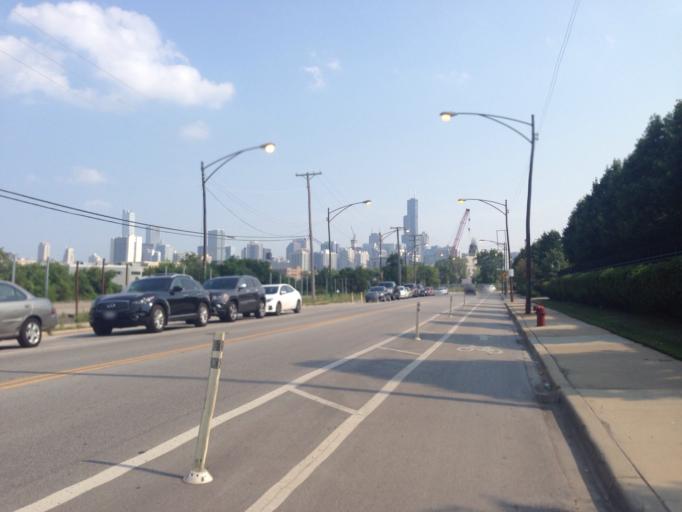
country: US
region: Illinois
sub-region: Cook County
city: Chicago
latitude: 41.9028
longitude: -87.6576
